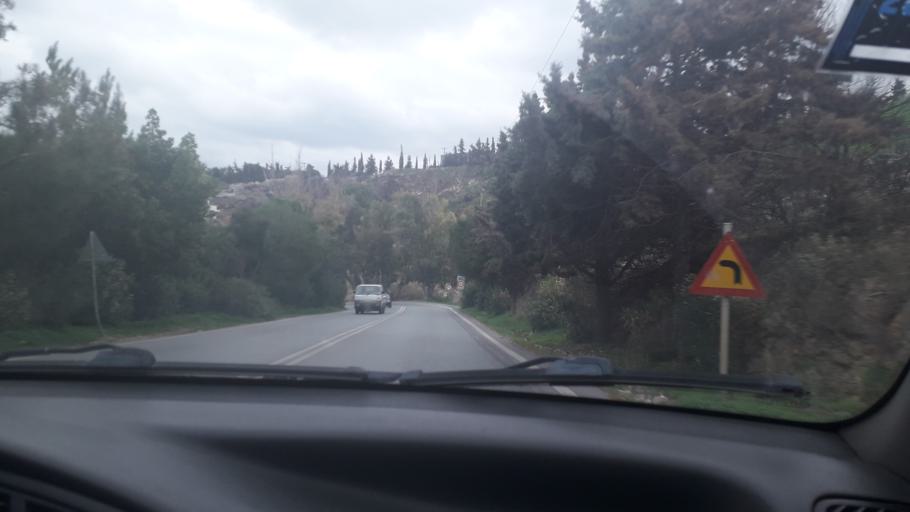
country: GR
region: Crete
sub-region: Nomos Rethymnis
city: Rethymno
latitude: 35.3573
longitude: 24.4704
